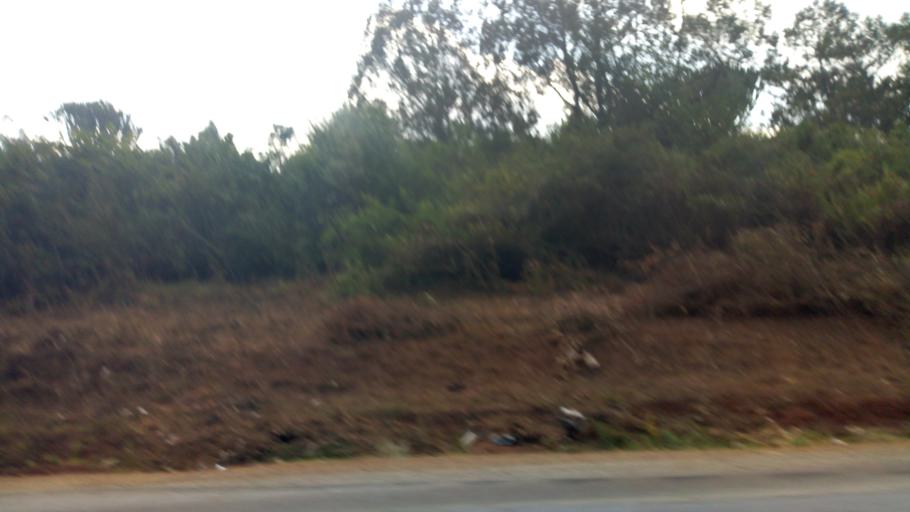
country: KE
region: Kiambu
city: Limuru
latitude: -1.0696
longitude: 36.6017
